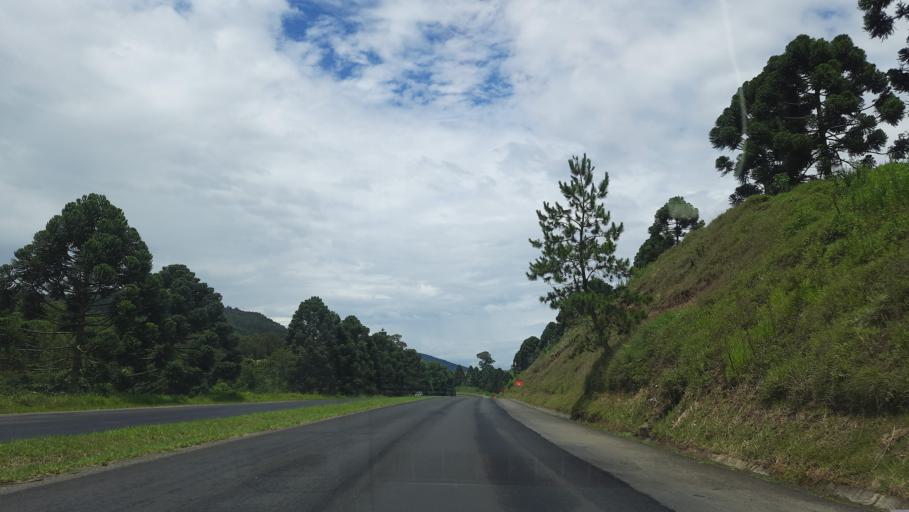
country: BR
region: Minas Gerais
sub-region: Pocos De Caldas
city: Pocos de Caldas
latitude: -21.8120
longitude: -46.6581
